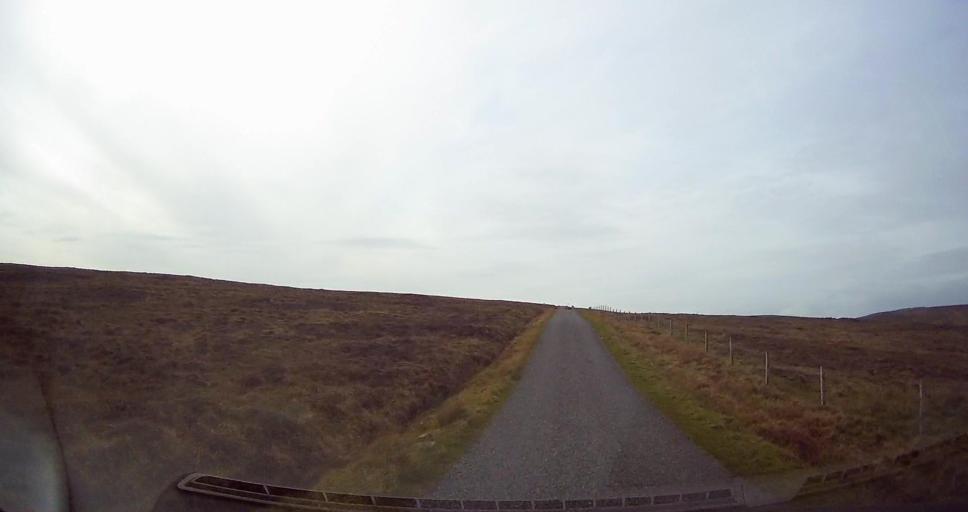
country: GB
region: Scotland
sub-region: Shetland Islands
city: Shetland
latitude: 60.1510
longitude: -1.0846
